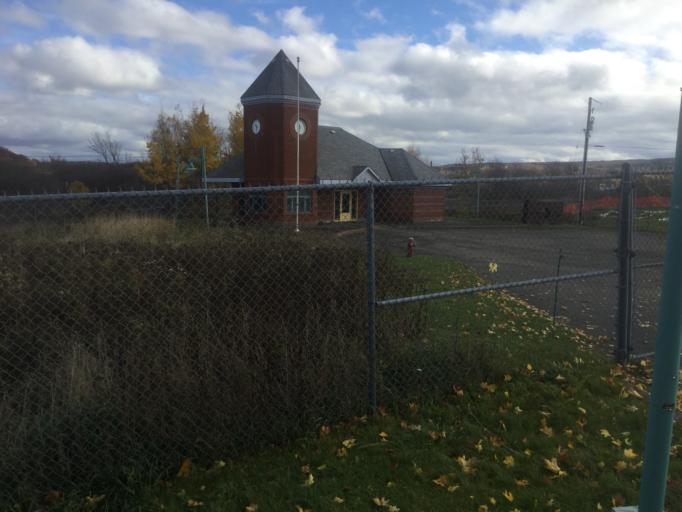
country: CA
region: Nova Scotia
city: New Glasgow
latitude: 45.5682
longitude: -62.6560
